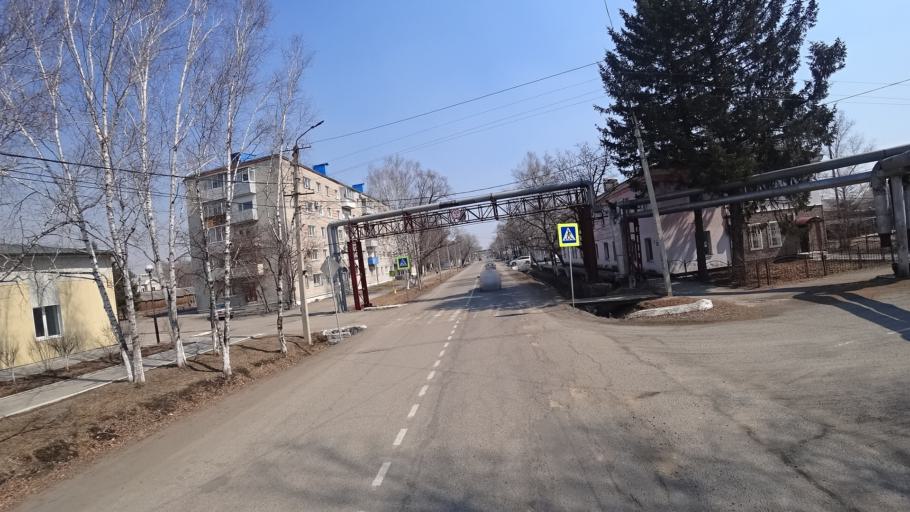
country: RU
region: Amur
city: Novobureyskiy
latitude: 49.7933
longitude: 129.8748
